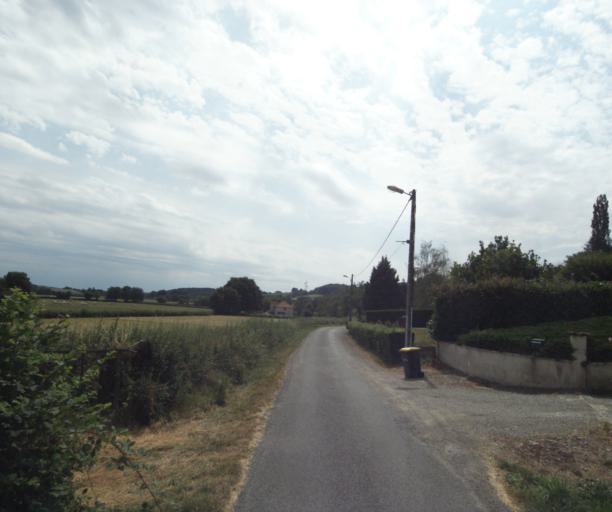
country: FR
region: Bourgogne
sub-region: Departement de Saone-et-Loire
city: Gueugnon
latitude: 46.6162
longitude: 4.0454
